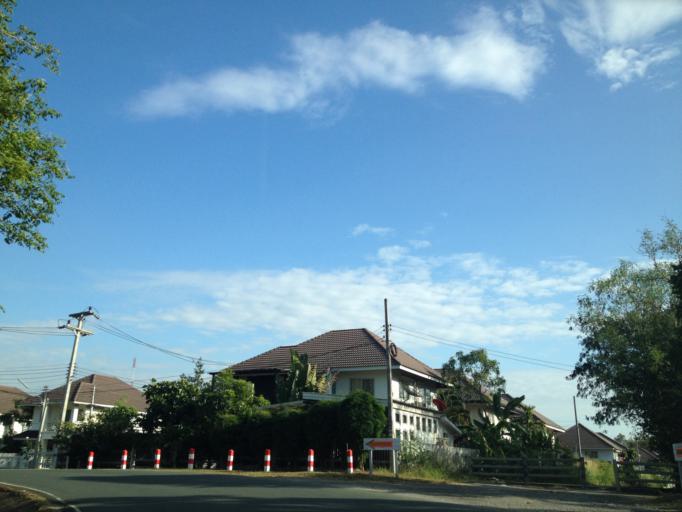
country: TH
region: Chiang Mai
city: Chiang Mai
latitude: 18.8578
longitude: 98.9518
